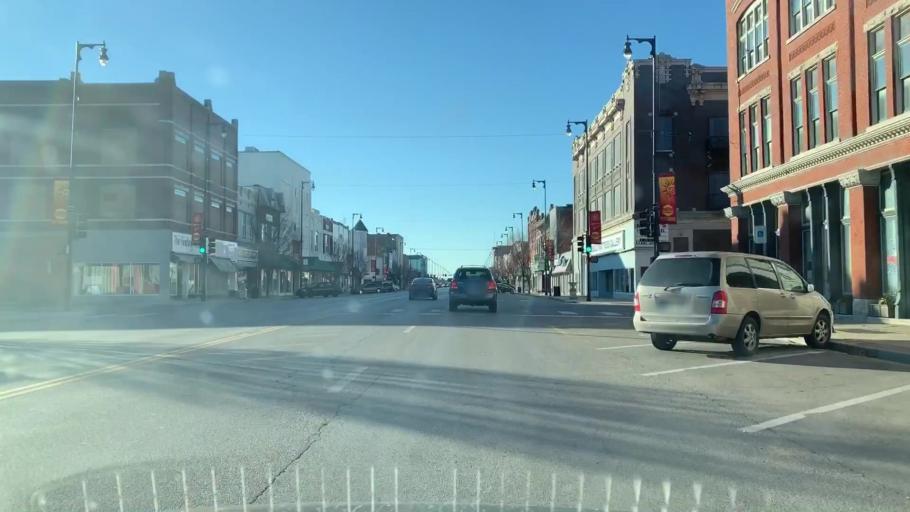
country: US
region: Kansas
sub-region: Crawford County
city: Pittsburg
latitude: 37.4144
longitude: -94.7049
